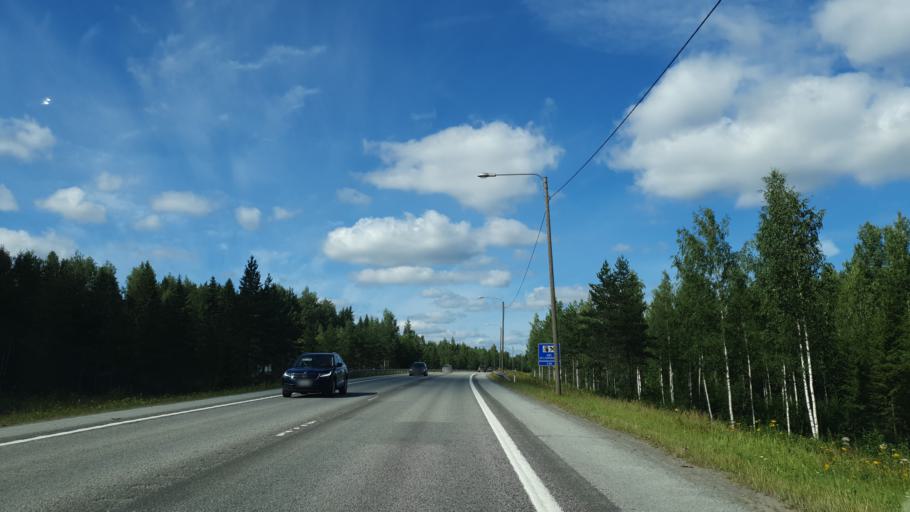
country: FI
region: Central Finland
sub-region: Jyvaeskylae
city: Muurame
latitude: 62.1710
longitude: 25.6809
